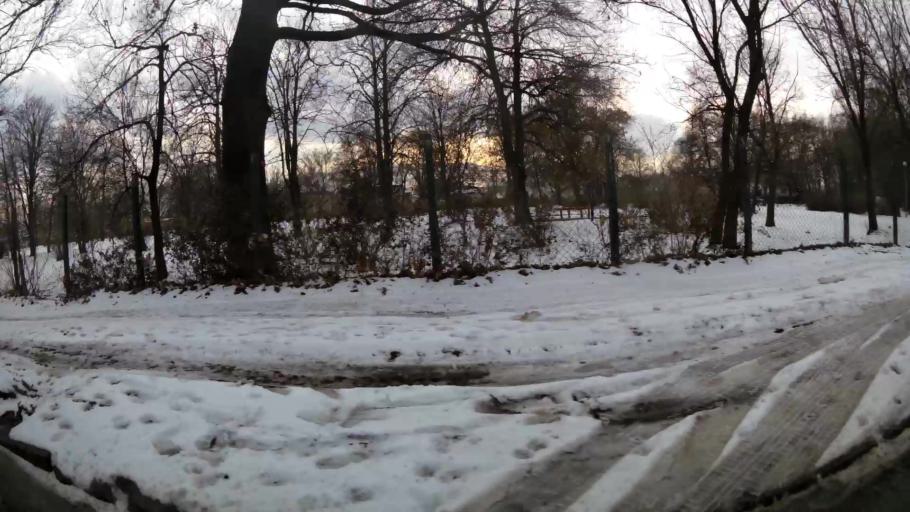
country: BG
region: Sofia-Capital
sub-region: Stolichna Obshtina
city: Sofia
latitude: 42.7267
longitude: 23.3398
